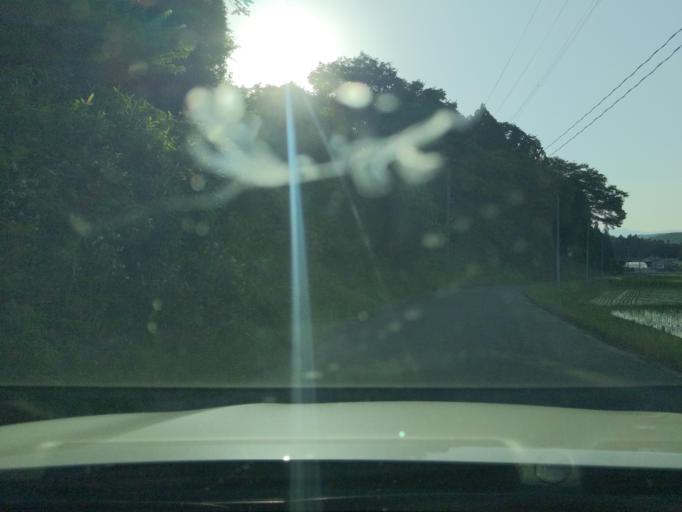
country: JP
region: Fukushima
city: Motomiya
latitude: 37.4676
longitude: 140.3331
